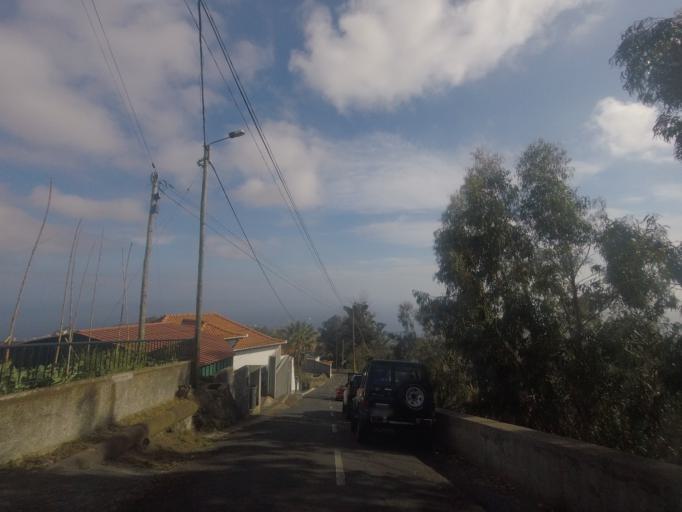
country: PT
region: Madeira
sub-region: Camara de Lobos
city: Curral das Freiras
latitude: 32.6780
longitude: -16.9538
